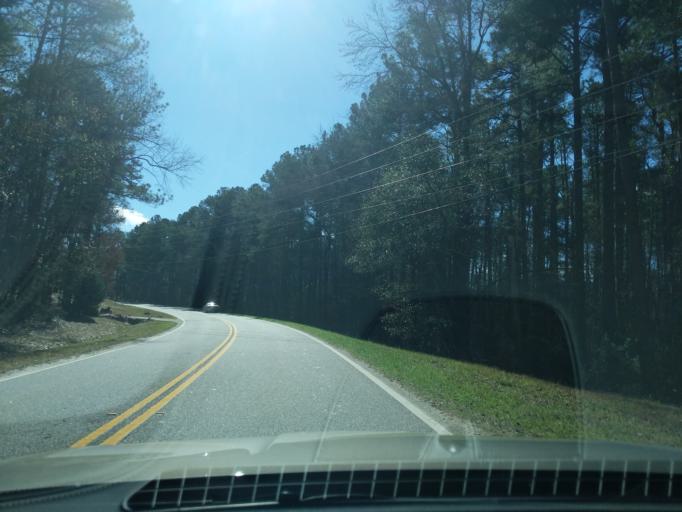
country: US
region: Georgia
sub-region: Columbia County
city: Evans
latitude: 33.5453
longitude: -82.1658
